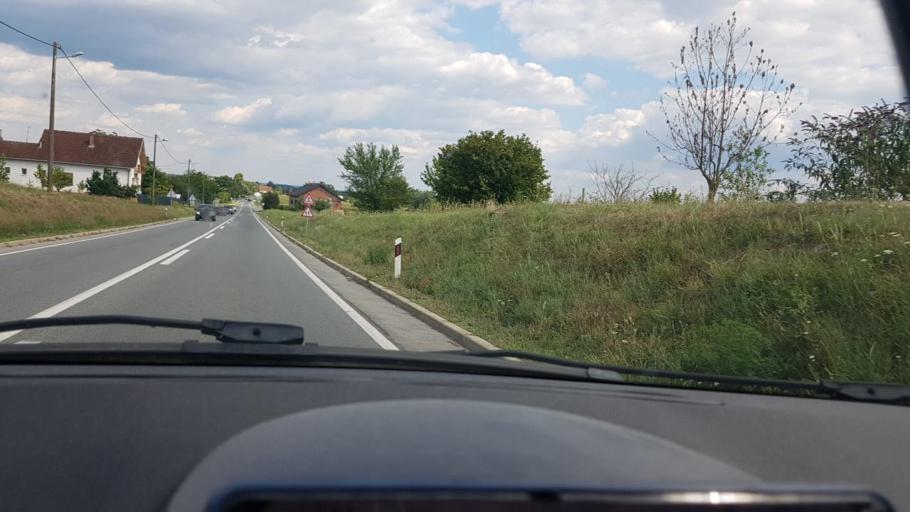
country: HR
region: Bjelovarsko-Bilogorska
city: Zdralovi
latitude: 45.8717
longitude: 16.8961
